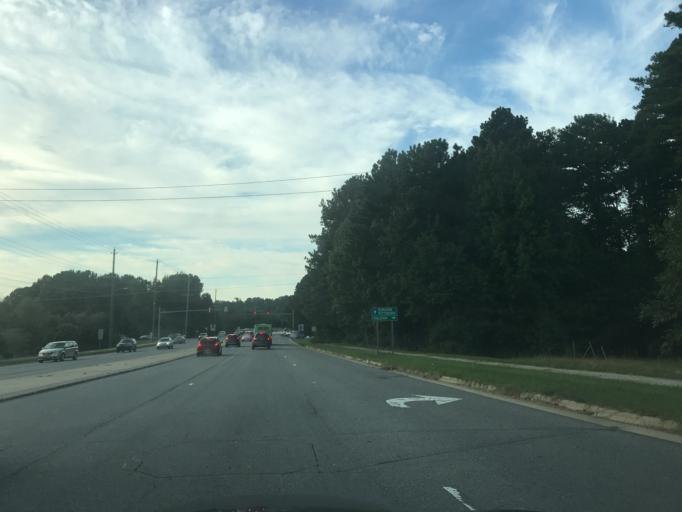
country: US
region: North Carolina
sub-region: Wake County
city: Apex
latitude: 35.7463
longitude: -78.8734
